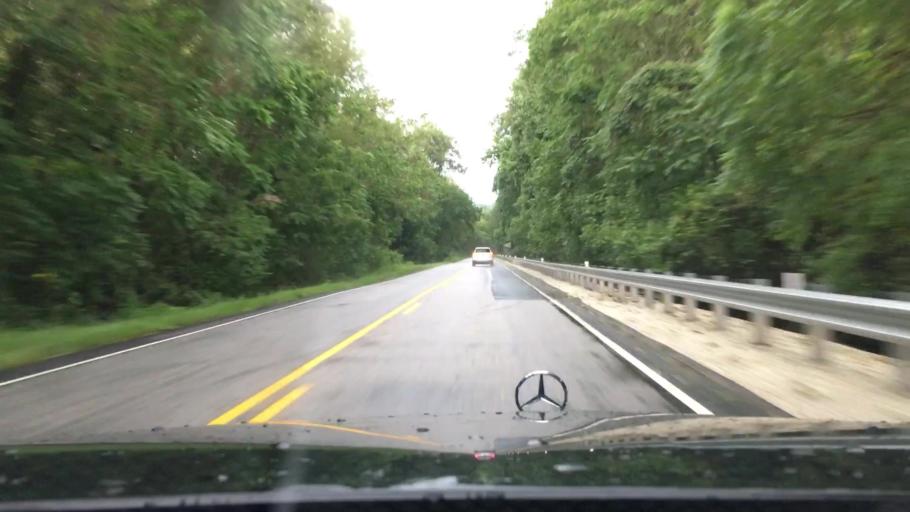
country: US
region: Virginia
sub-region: Amherst County
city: Amherst
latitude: 37.6779
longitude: -79.0193
